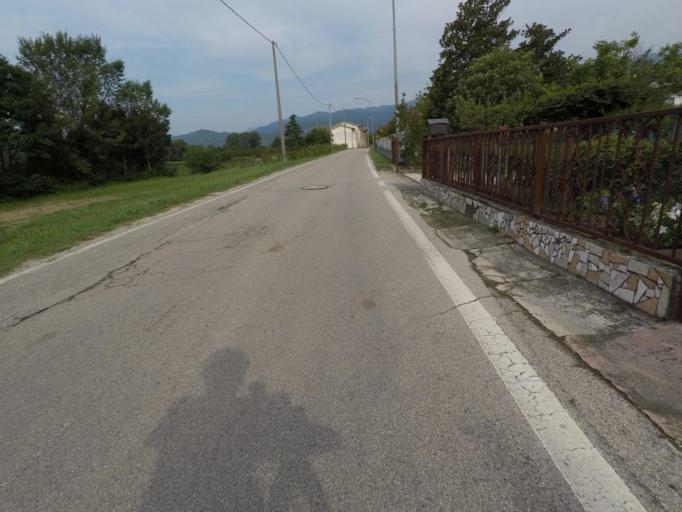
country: IT
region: Veneto
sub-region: Provincia di Treviso
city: Cappella Maggiore
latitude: 45.9691
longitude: 12.3405
